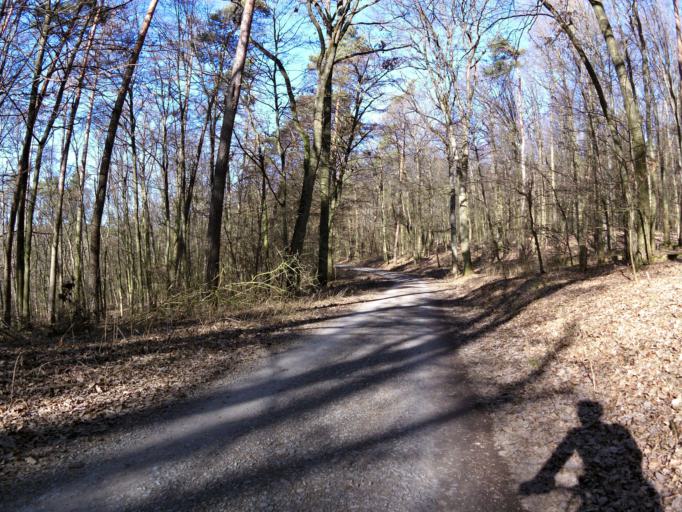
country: DE
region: Bavaria
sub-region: Regierungsbezirk Unterfranken
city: Rimpar
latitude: 49.8517
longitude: 9.9860
